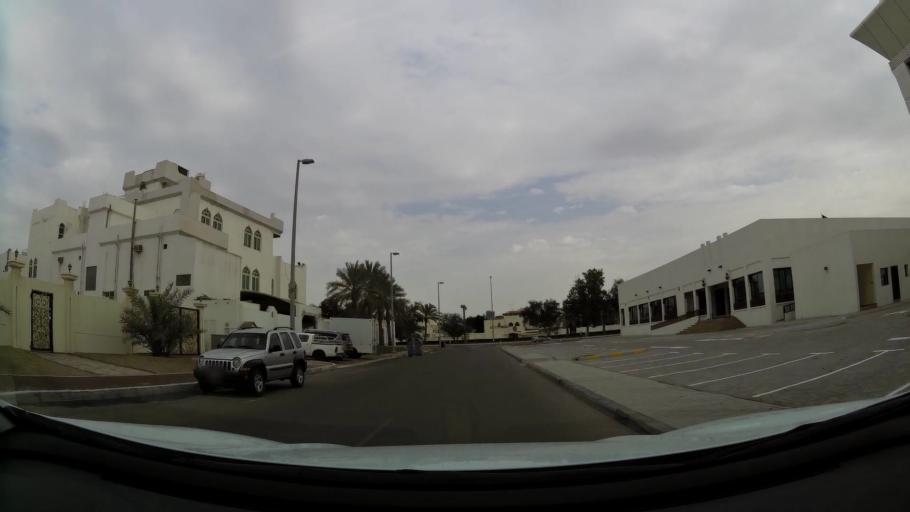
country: AE
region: Abu Dhabi
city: Abu Dhabi
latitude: 24.4261
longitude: 54.4097
